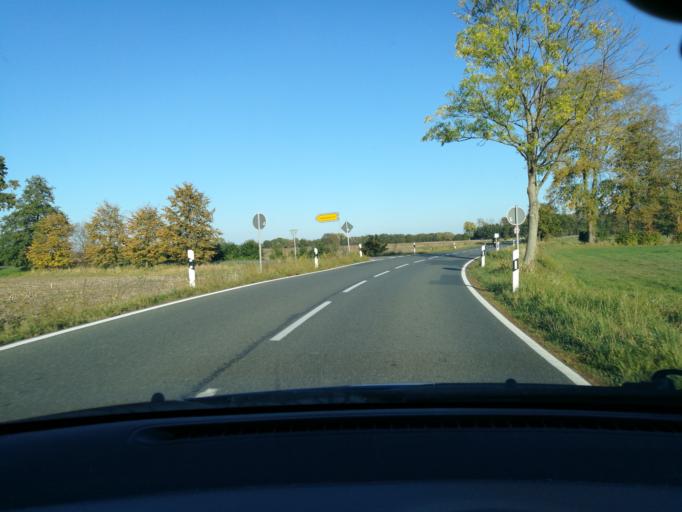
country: DE
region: Lower Saxony
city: Neetze
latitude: 53.3174
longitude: 10.6375
